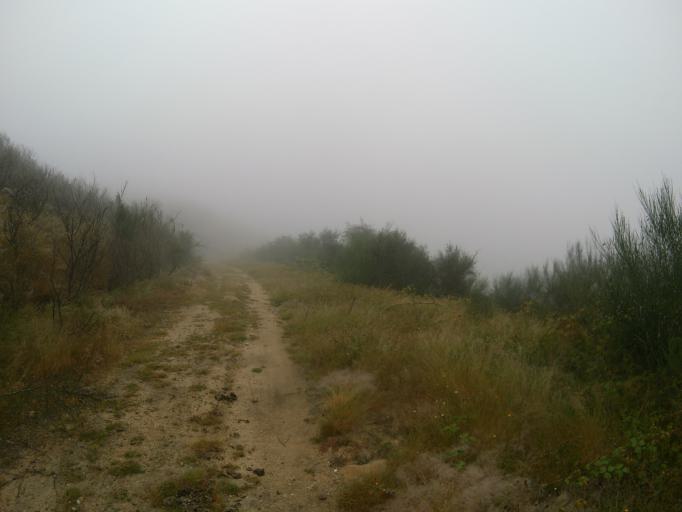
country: PT
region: Viana do Castelo
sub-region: Ponte de Lima
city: Ponte de Lima
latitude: 41.6971
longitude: -8.6089
